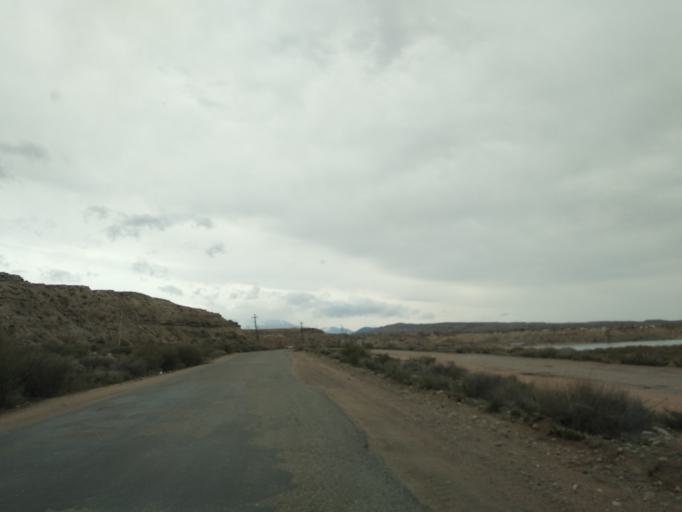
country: KG
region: Ysyk-Koel
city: Bokombayevskoye
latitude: 42.1578
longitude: 77.0668
